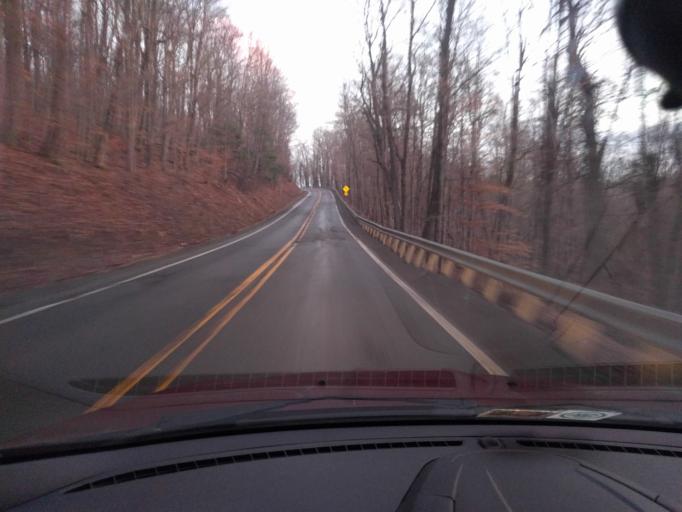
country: US
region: West Virginia
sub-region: Greenbrier County
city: Rainelle
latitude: 37.9894
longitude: -80.8605
